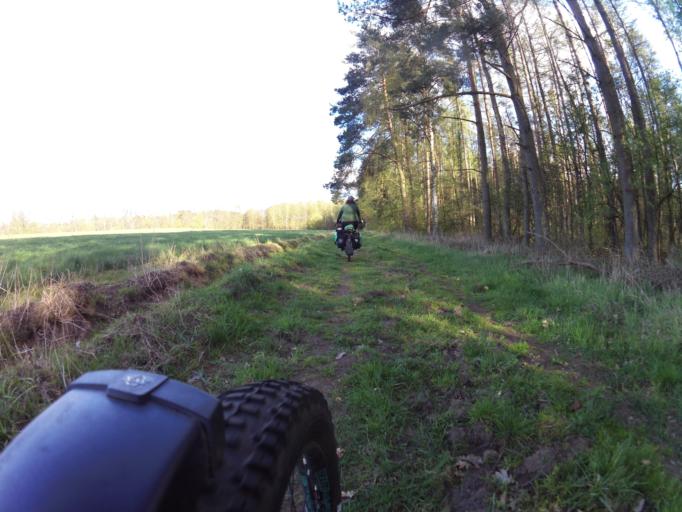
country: PL
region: West Pomeranian Voivodeship
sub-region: Powiat gryficki
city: Ploty
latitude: 53.7643
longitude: 15.2627
